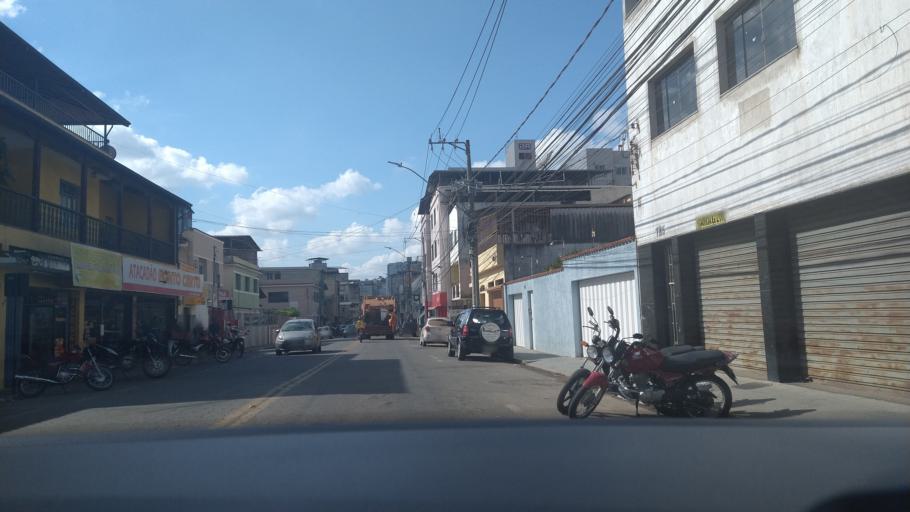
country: BR
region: Minas Gerais
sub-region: Vicosa
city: Vicosa
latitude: -20.7630
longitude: -42.8810
